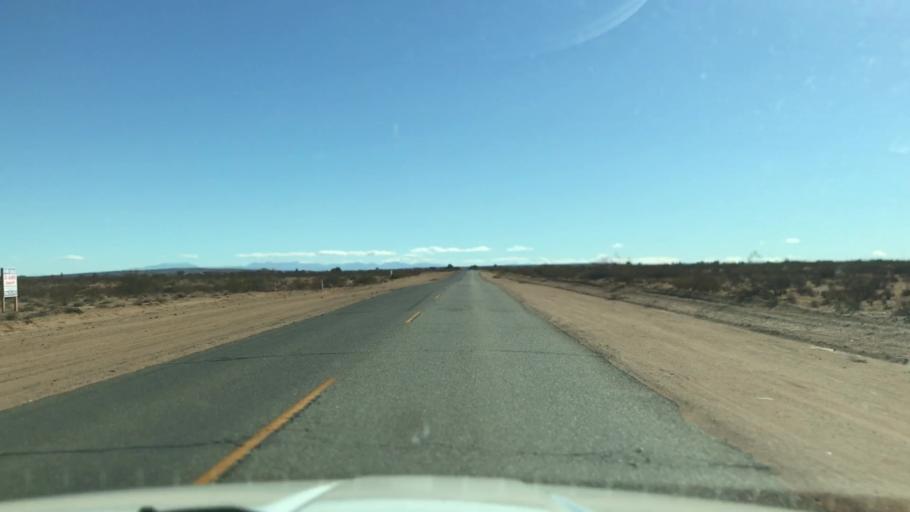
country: US
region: California
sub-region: Kern County
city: California City
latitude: 35.1544
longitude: -117.9859
